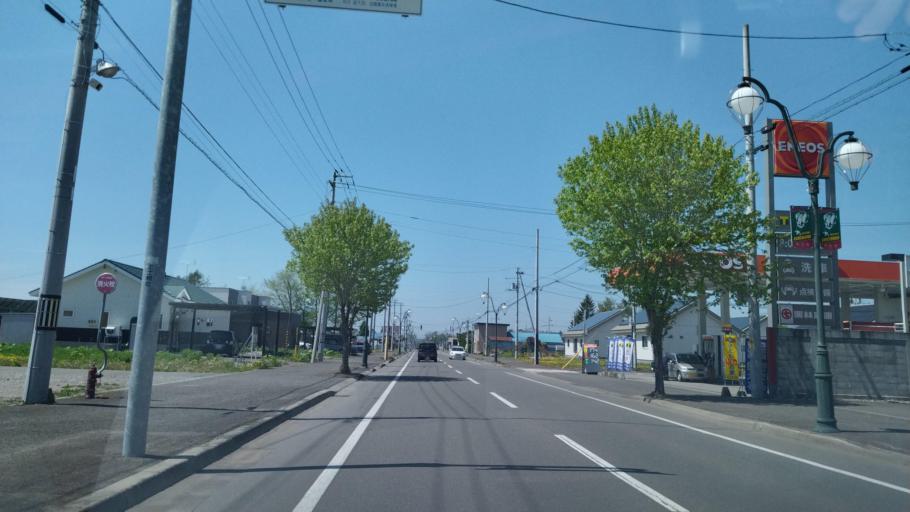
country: JP
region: Hokkaido
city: Otofuke
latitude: 43.2330
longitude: 143.2898
